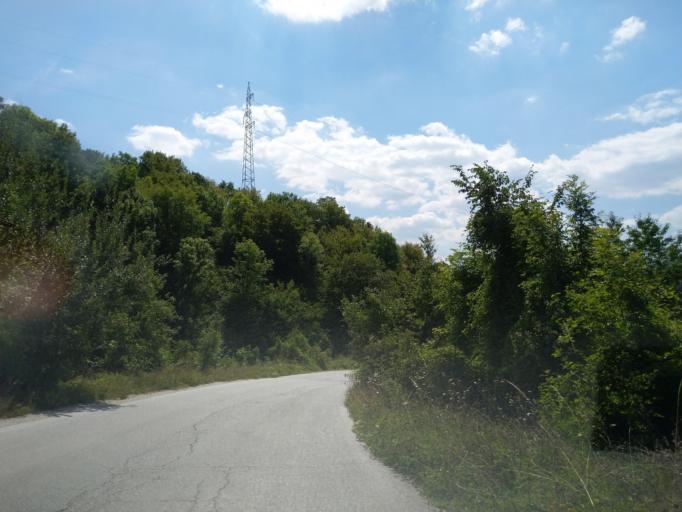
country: RS
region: Central Serbia
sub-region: Zlatiborski Okrug
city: Nova Varos
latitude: 43.4209
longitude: 19.9363
